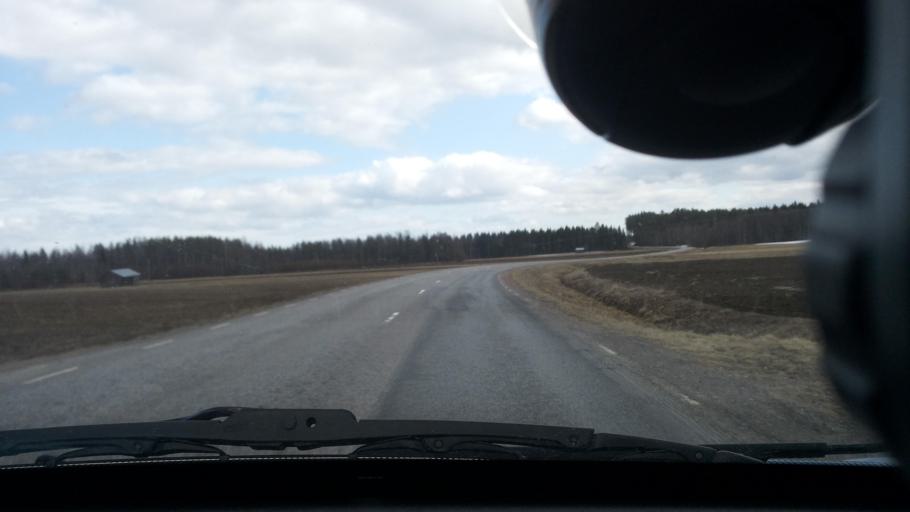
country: SE
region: Norrbotten
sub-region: Bodens Kommun
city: Saevast
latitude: 65.6728
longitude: 21.8046
